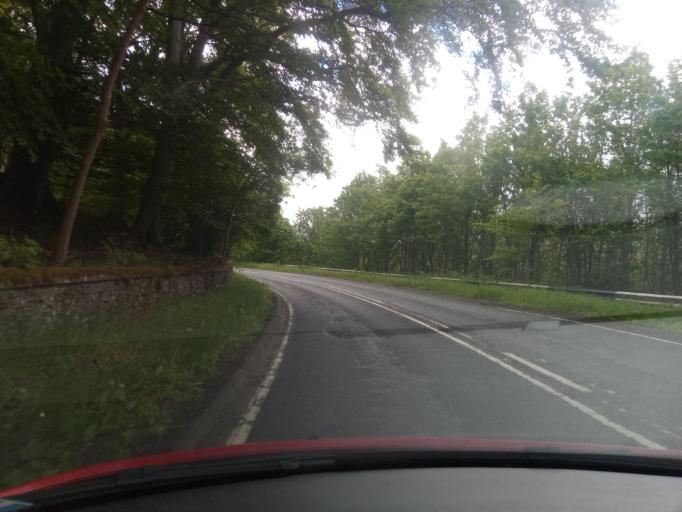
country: GB
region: Scotland
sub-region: The Scottish Borders
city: Galashiels
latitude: 55.6840
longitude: -2.8691
